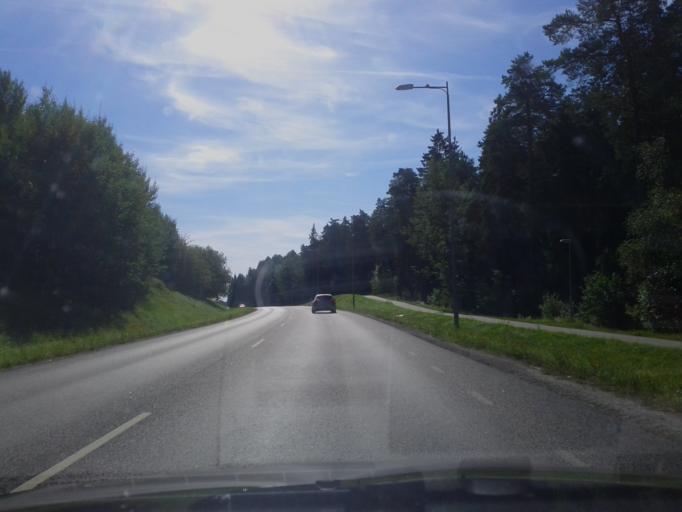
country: SE
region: Stockholm
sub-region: Taby Kommun
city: Taby
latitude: 59.4588
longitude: 18.0785
